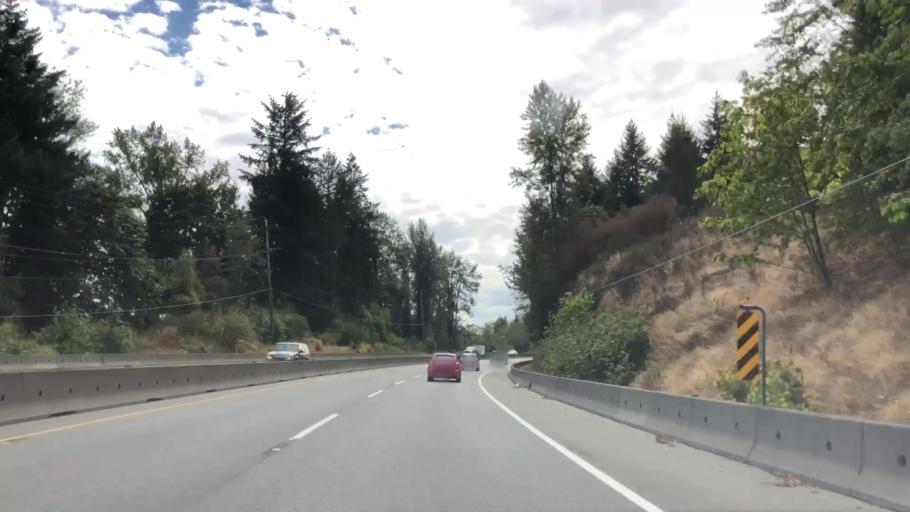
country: CA
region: British Columbia
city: North Cowichan
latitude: 48.8674
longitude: -123.7113
